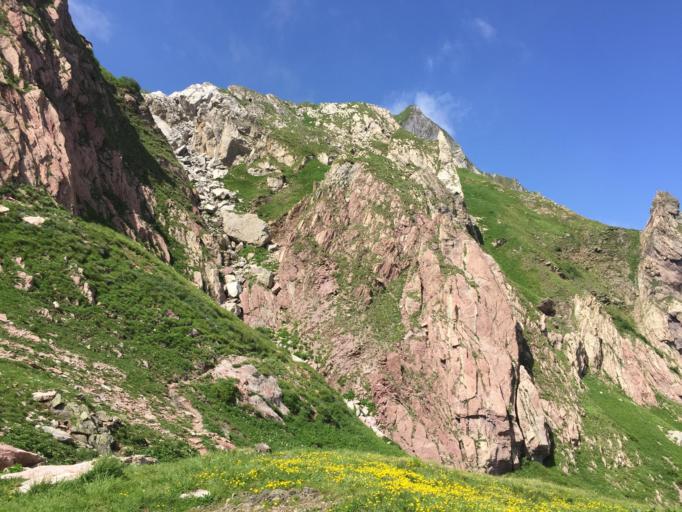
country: IT
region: Friuli Venezia Giulia
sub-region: Provincia di Udine
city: Rigolato
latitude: 46.6142
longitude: 12.8808
